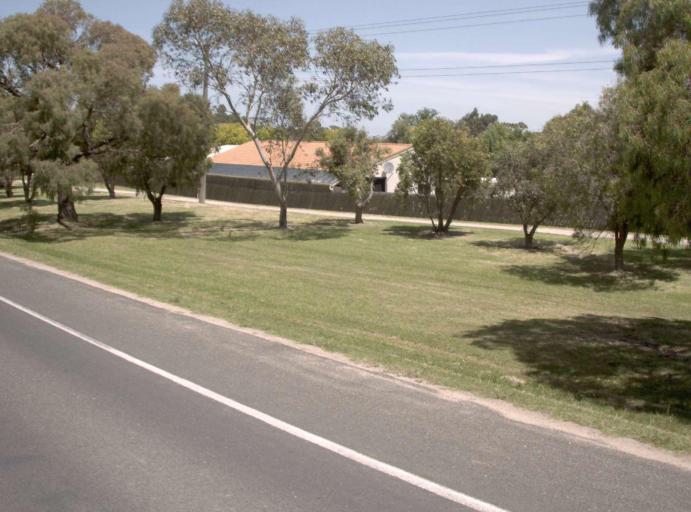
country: AU
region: Victoria
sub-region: East Gippsland
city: Bairnsdale
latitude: -37.8177
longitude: 147.6489
